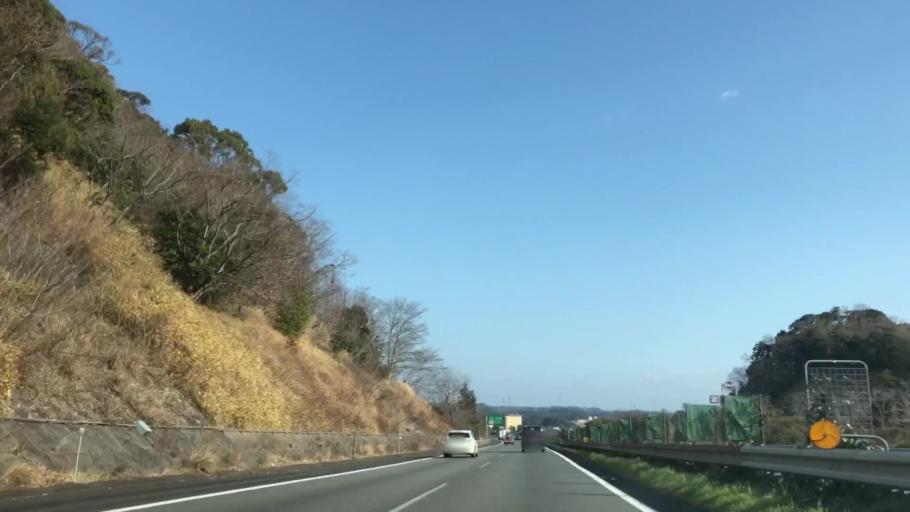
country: JP
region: Shizuoka
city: Kakegawa
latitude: 34.7534
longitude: 138.0753
